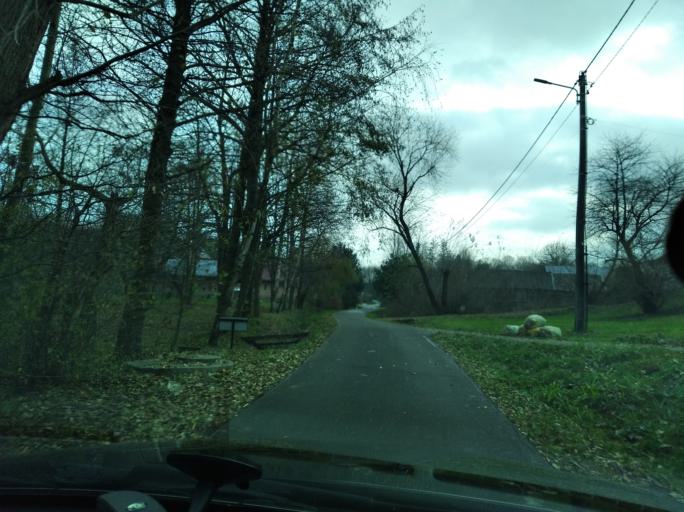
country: PL
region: Subcarpathian Voivodeship
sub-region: Powiat przeworski
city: Sietesz
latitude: 50.0027
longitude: 22.3520
